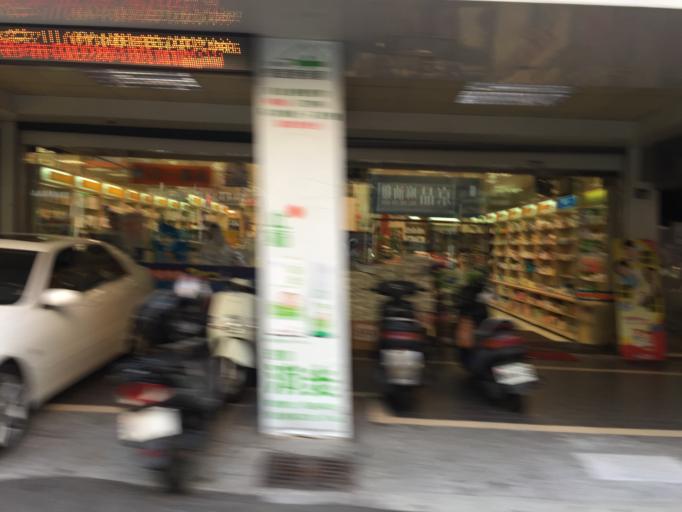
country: TW
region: Taiwan
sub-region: Hsinchu
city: Hsinchu
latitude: 24.8059
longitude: 120.9626
